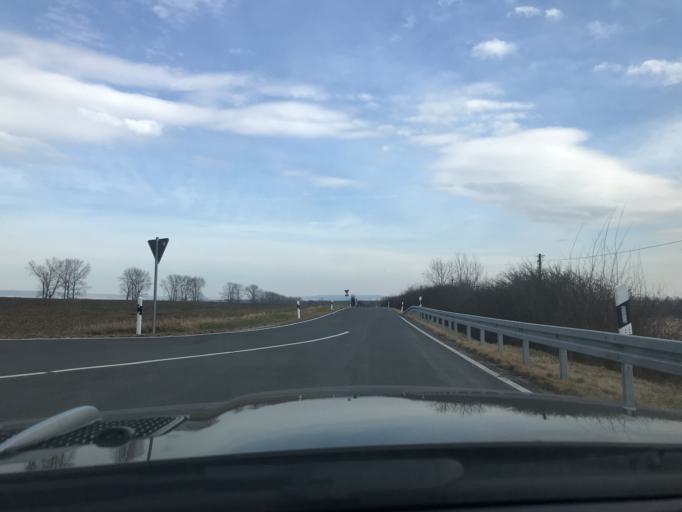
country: DE
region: Thuringia
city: Oberdorla
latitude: 51.1812
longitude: 10.4010
